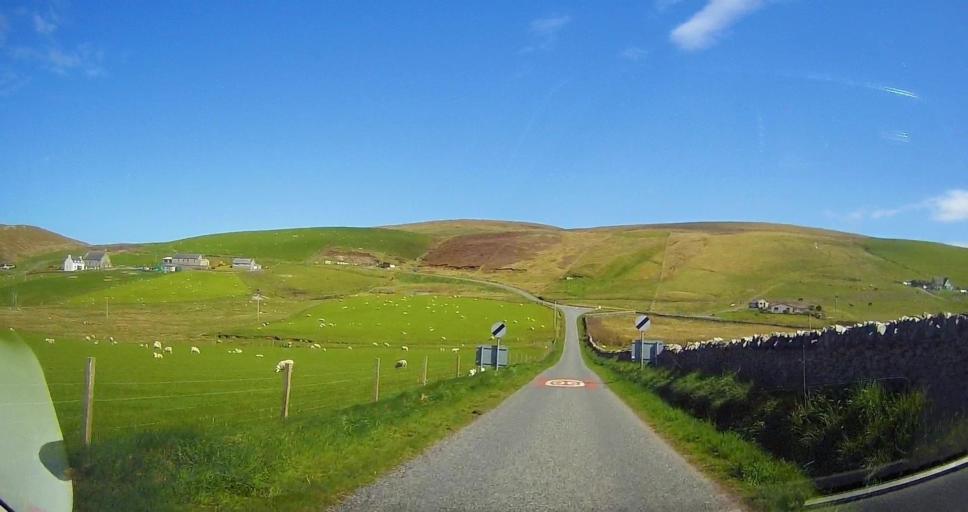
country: GB
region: Scotland
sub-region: Shetland Islands
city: Sandwick
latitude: 59.9727
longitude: -1.3199
